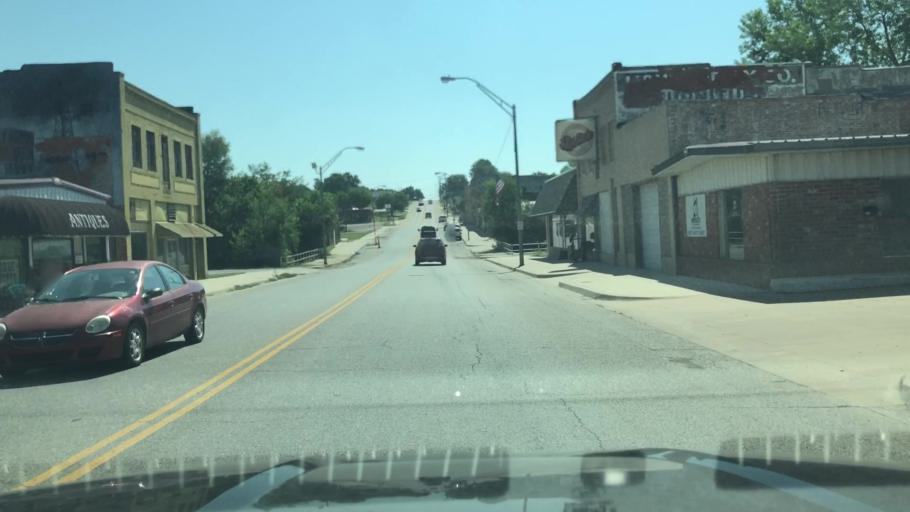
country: US
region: Oklahoma
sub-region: Creek County
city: Drumright
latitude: 35.9884
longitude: -96.5979
